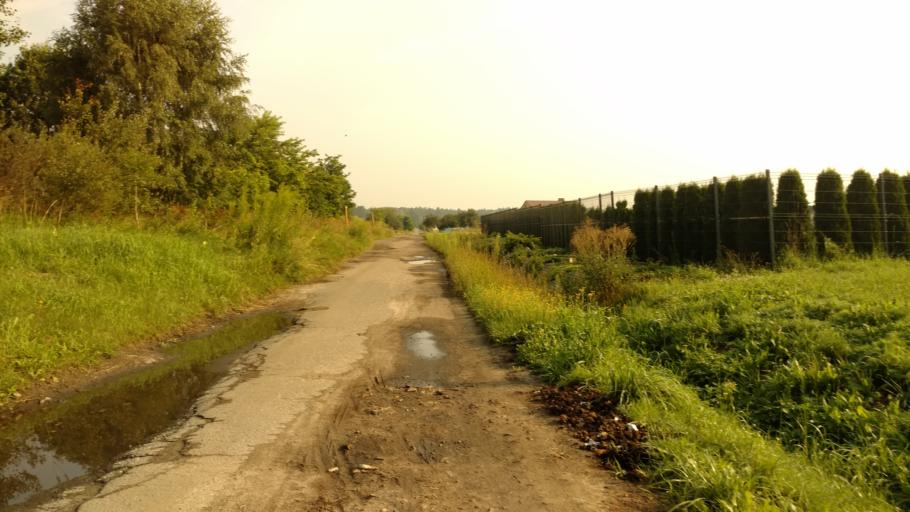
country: PL
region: Silesian Voivodeship
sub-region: Powiat pszczynski
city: Jankowice
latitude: 50.0219
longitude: 18.9754
